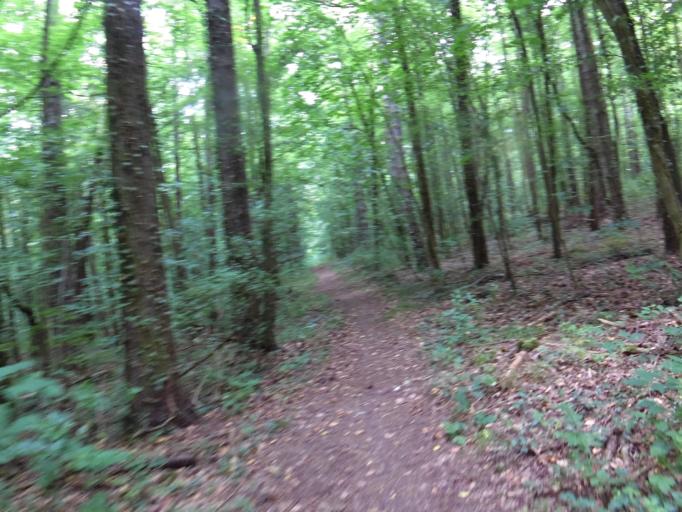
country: DE
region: Bavaria
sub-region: Regierungsbezirk Unterfranken
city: Reichenberg
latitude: 49.7655
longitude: 9.9177
